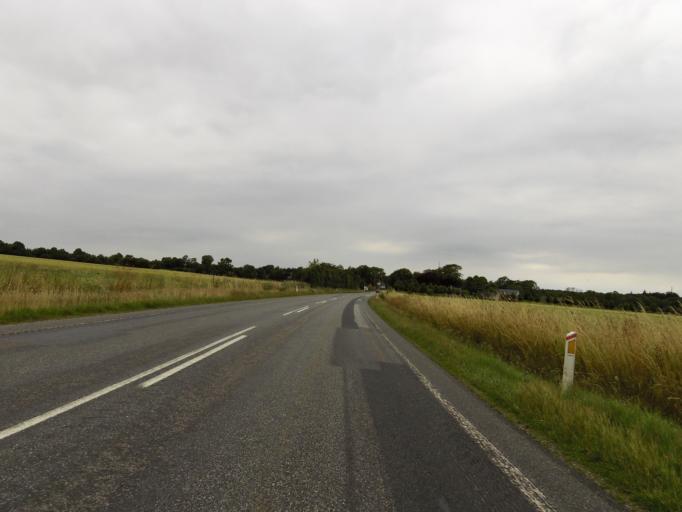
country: DK
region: South Denmark
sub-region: Tonder Kommune
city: Logumkloster
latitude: 55.1455
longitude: 8.9633
